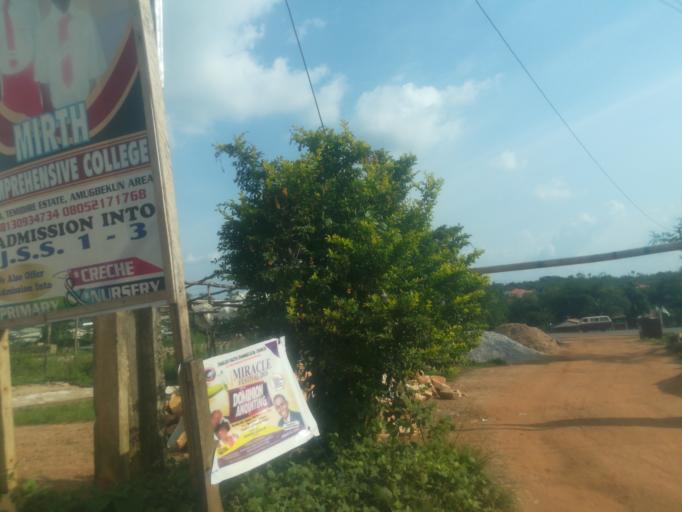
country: NG
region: Oyo
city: Ido
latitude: 7.3973
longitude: 3.7937
